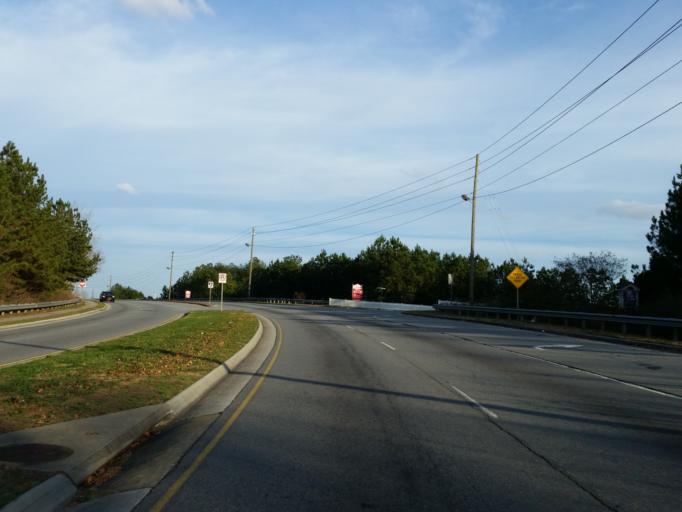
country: US
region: Georgia
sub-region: Cobb County
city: Powder Springs
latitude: 33.8665
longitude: -84.6926
